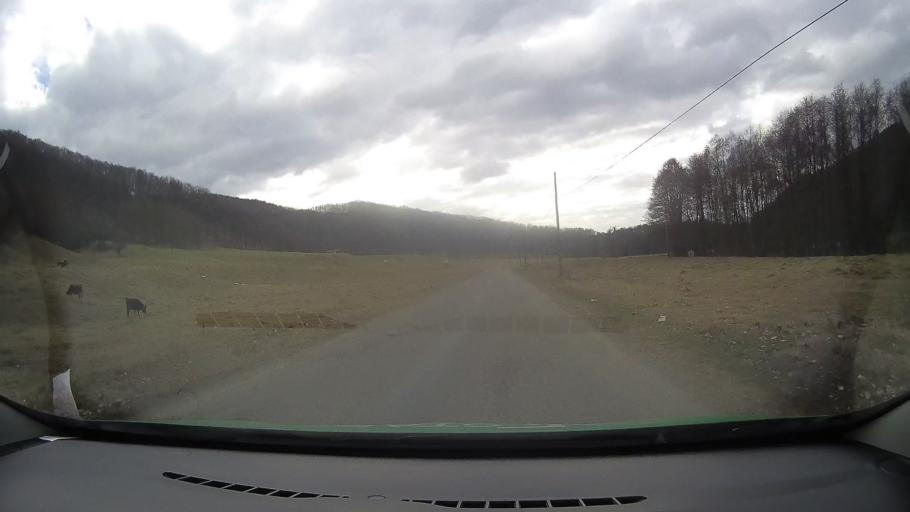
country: RO
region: Dambovita
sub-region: Comuna Visinesti
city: Visinesti
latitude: 45.0936
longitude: 25.5787
